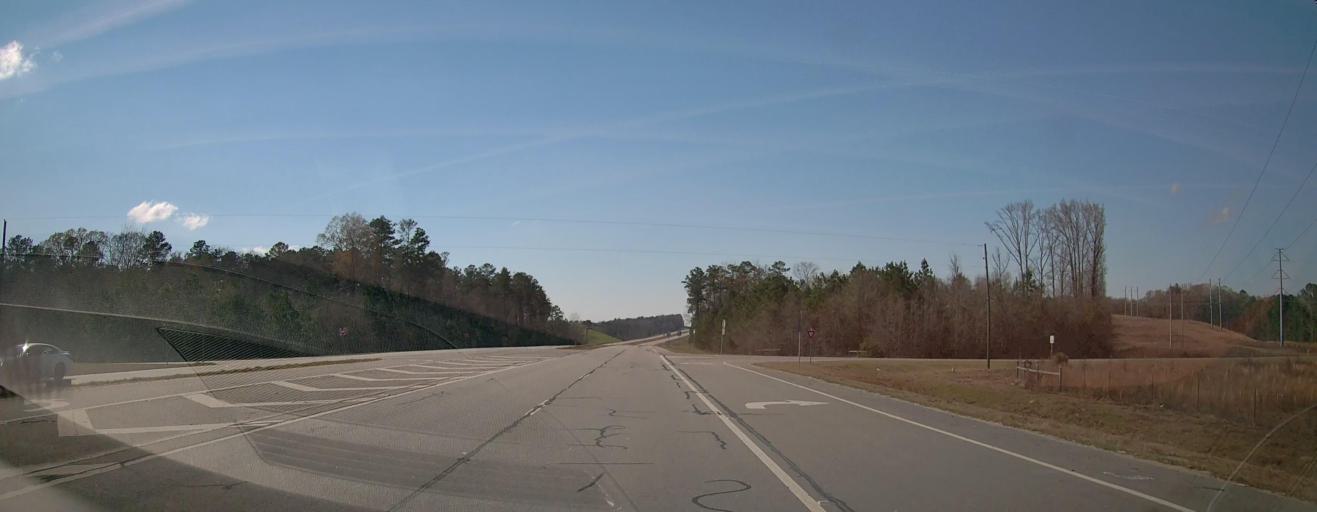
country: US
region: Georgia
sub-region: Wilkinson County
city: Gordon
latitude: 32.8968
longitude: -83.3253
